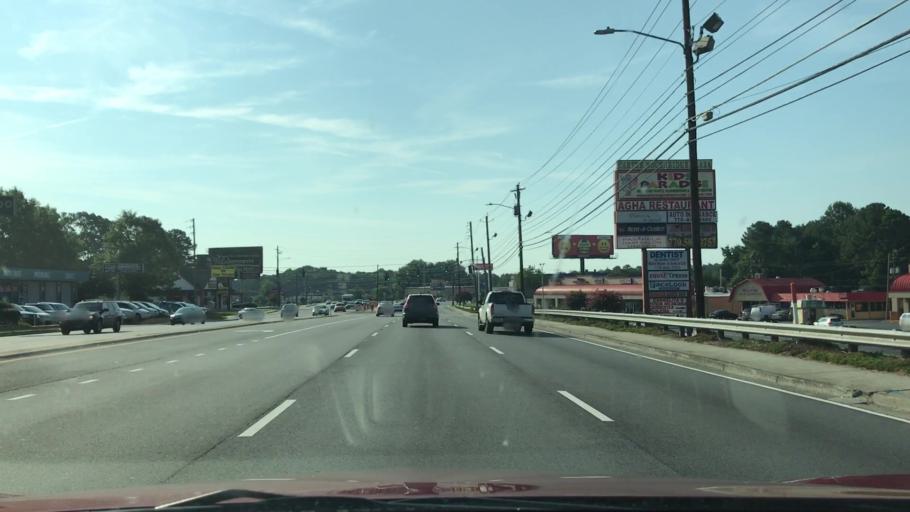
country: US
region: Georgia
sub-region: Gwinnett County
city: Norcross
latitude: 33.8975
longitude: -84.1999
